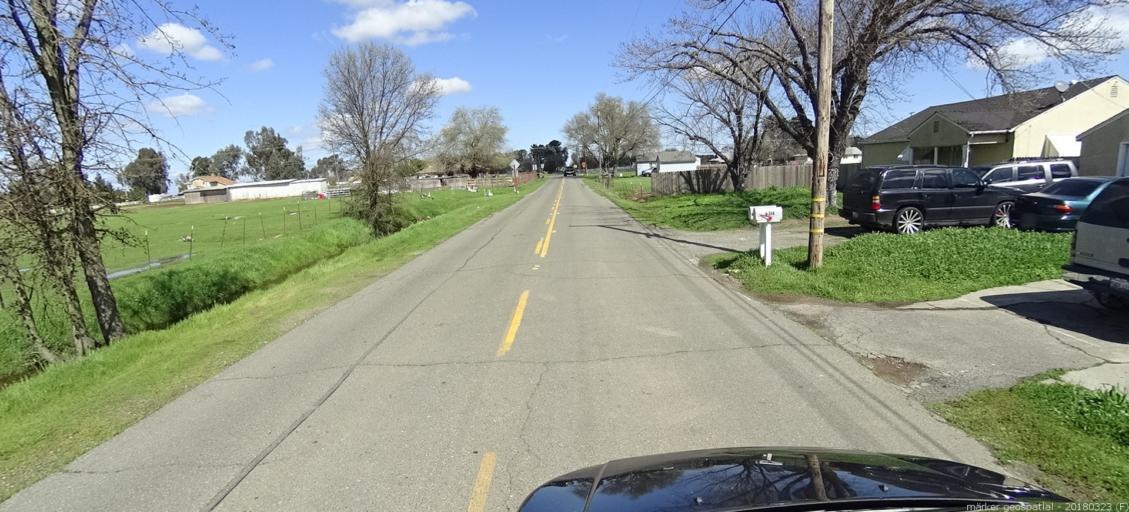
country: US
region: California
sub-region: Sacramento County
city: Rio Linda
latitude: 38.6822
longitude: -121.4153
